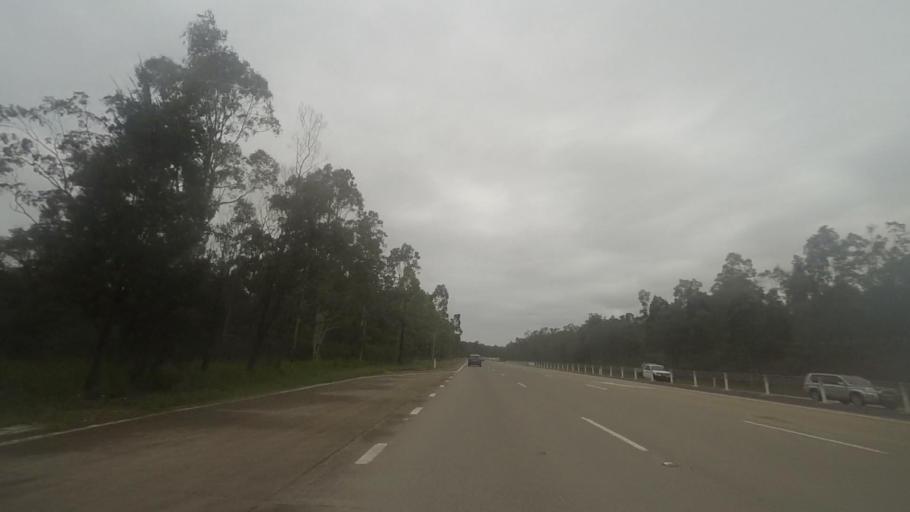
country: AU
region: New South Wales
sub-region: Port Stephens Shire
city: Medowie
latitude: -32.6891
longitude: 151.8093
